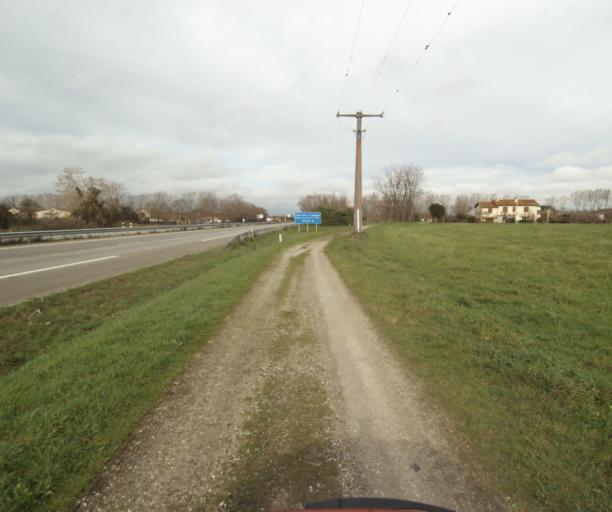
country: FR
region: Midi-Pyrenees
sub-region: Departement de l'Ariege
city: La Tour-du-Crieu
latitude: 43.1144
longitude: 1.6310
